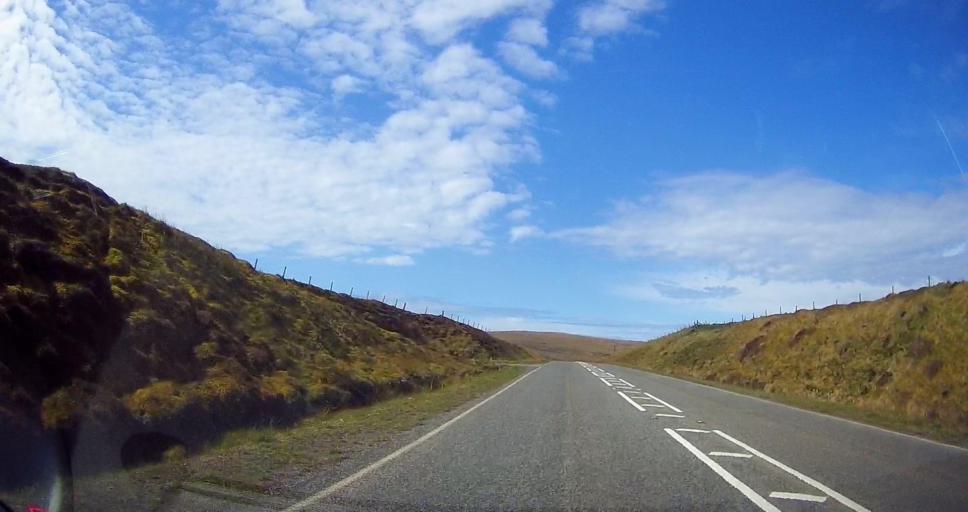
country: GB
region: Scotland
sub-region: Shetland Islands
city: Sandwick
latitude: 60.0099
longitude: -1.2644
